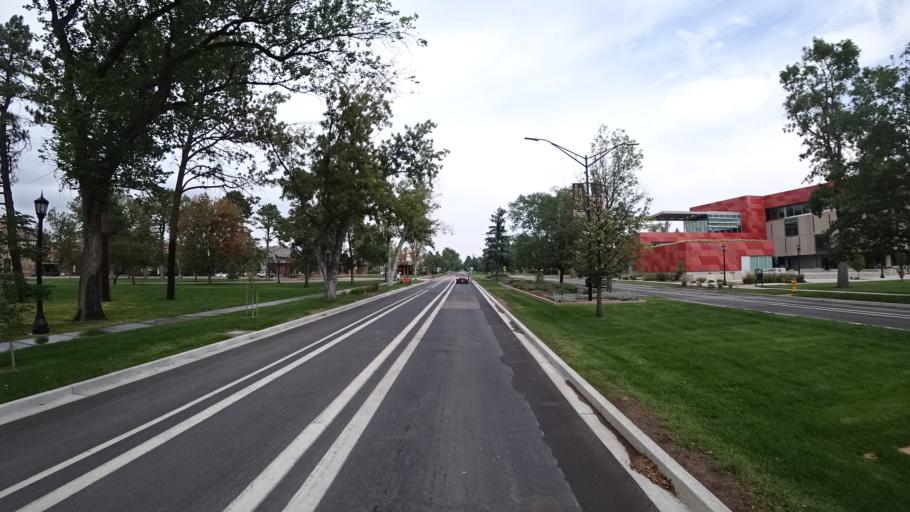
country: US
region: Colorado
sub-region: El Paso County
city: Colorado Springs
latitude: 38.8486
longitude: -104.8247
